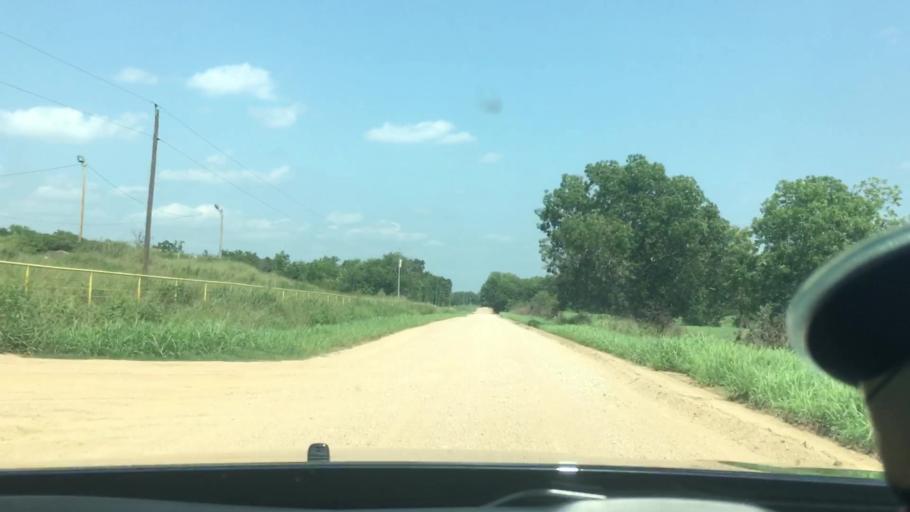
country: US
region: Oklahoma
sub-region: Coal County
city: Coalgate
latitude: 34.4295
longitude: -96.4569
